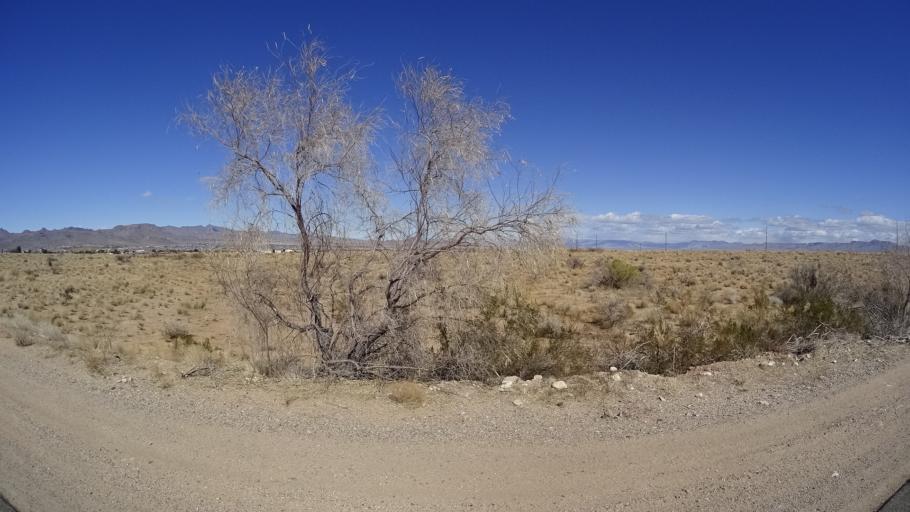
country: US
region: Arizona
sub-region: Mohave County
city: Kingman
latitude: 35.1959
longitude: -113.9902
